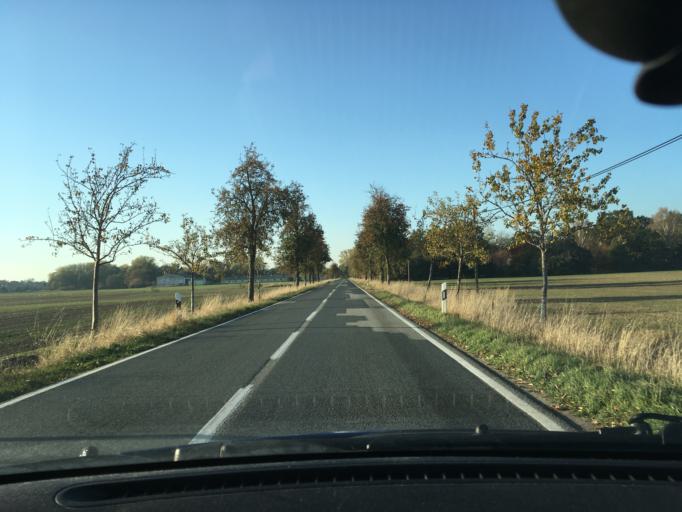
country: DE
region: Lower Saxony
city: Neu Darchau
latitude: 53.2912
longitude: 10.8700
